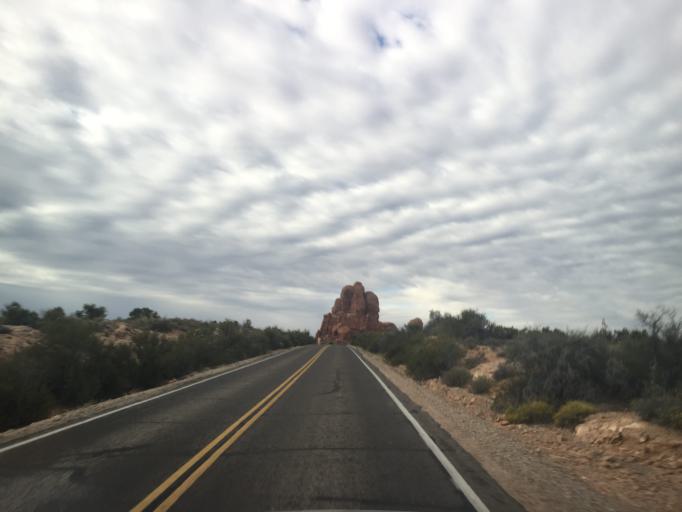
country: US
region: Utah
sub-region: Grand County
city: Moab
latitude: 38.7068
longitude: -109.5624
